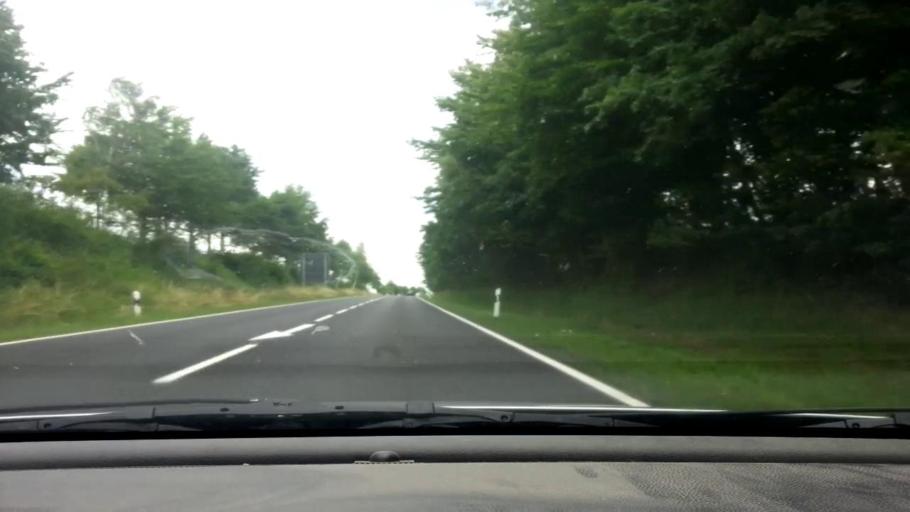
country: DE
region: Bavaria
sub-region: Upper Palatinate
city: Leonberg
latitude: 49.9785
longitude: 12.2719
